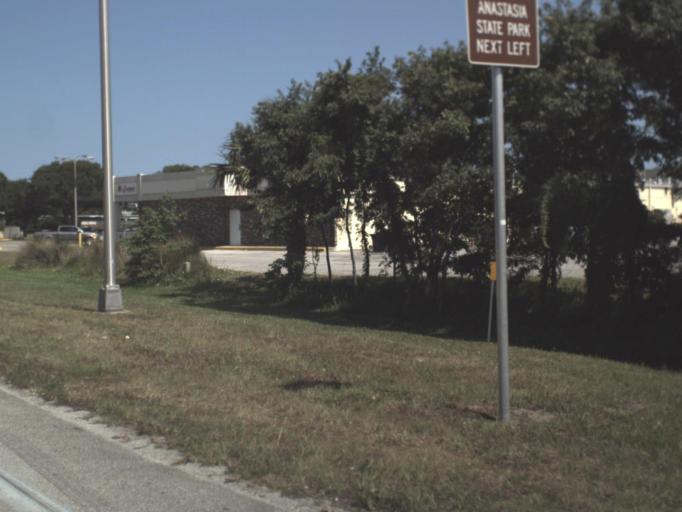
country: US
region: Florida
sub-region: Saint Johns County
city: Saint Augustine Beach
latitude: 29.8610
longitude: -81.2839
